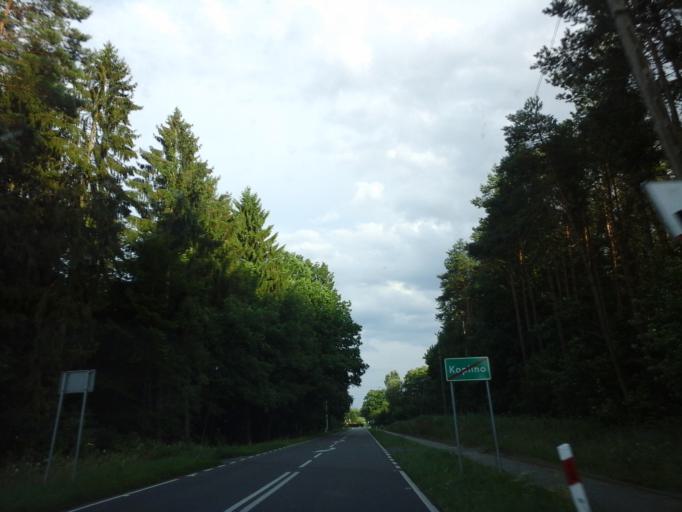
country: PL
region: West Pomeranian Voivodeship
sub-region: Powiat kamienski
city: Golczewo
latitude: 53.8658
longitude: 14.9054
